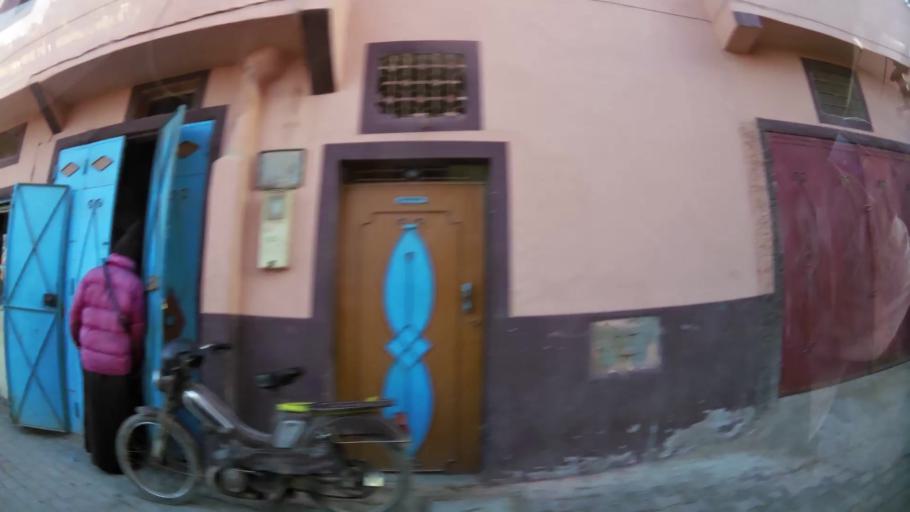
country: MA
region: Marrakech-Tensift-Al Haouz
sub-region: Kelaa-Des-Sraghna
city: Sidi Abdallah
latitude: 32.2452
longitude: -7.9490
